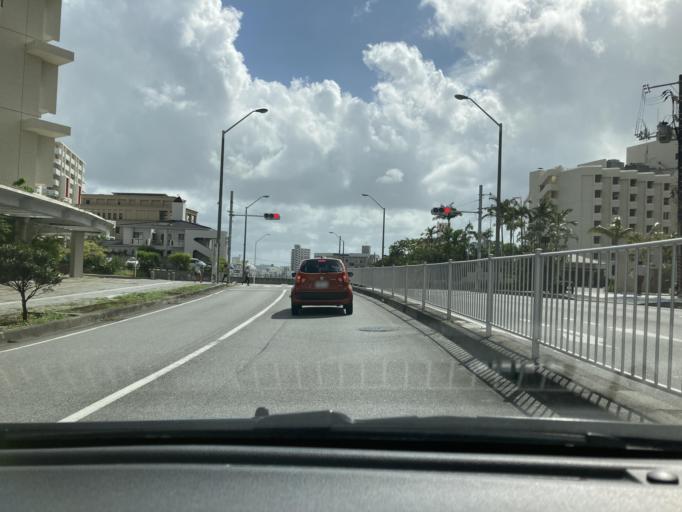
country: JP
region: Okinawa
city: Naha-shi
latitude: 26.2248
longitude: 127.6927
